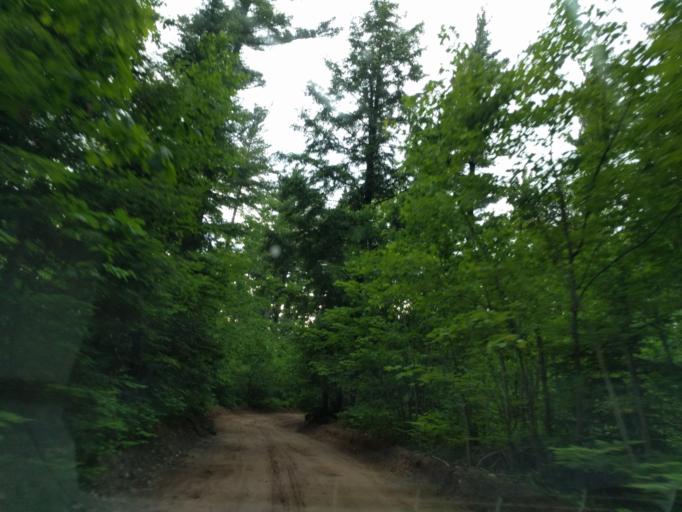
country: US
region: Michigan
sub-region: Marquette County
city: Trowbridge Park
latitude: 46.6071
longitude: -87.5072
